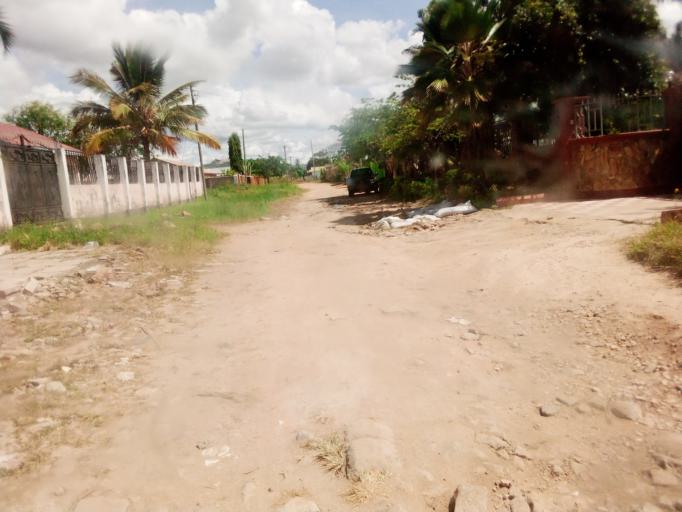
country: TZ
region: Dodoma
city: Dodoma
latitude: -6.1676
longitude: 35.7628
